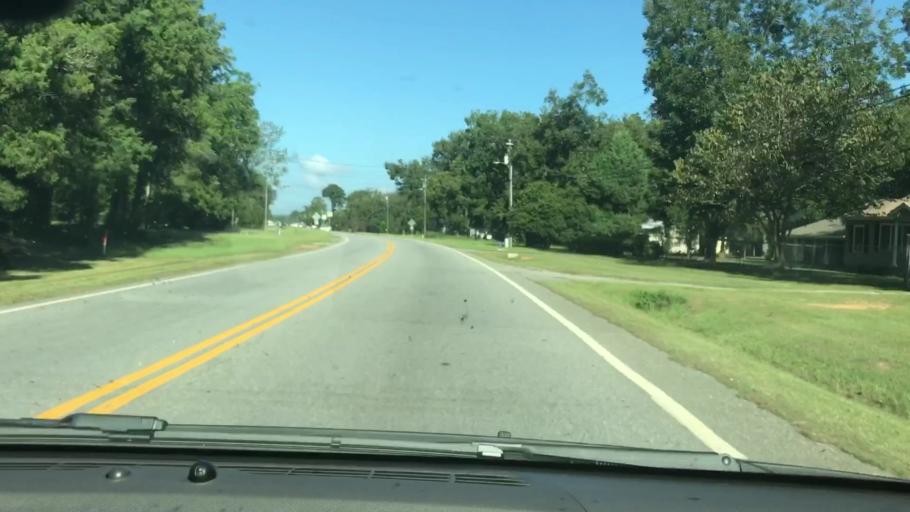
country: US
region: Georgia
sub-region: Quitman County
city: Georgetown
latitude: 31.8806
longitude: -85.0857
